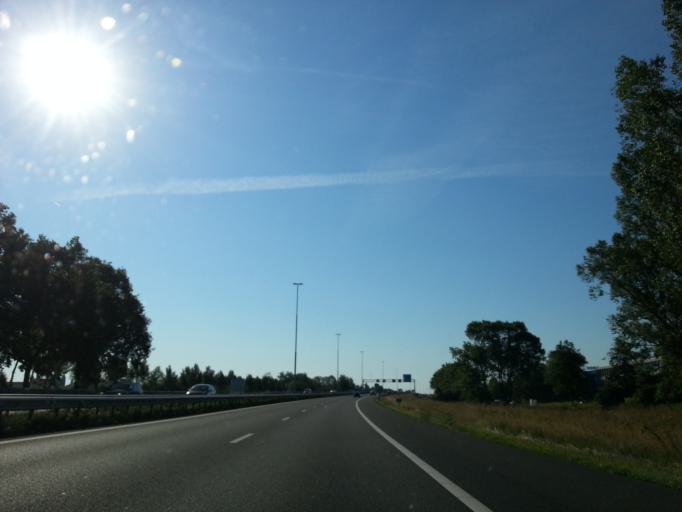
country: NL
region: North Brabant
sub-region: Gemeente Oirschot
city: Oirschot
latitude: 51.5029
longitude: 5.2918
